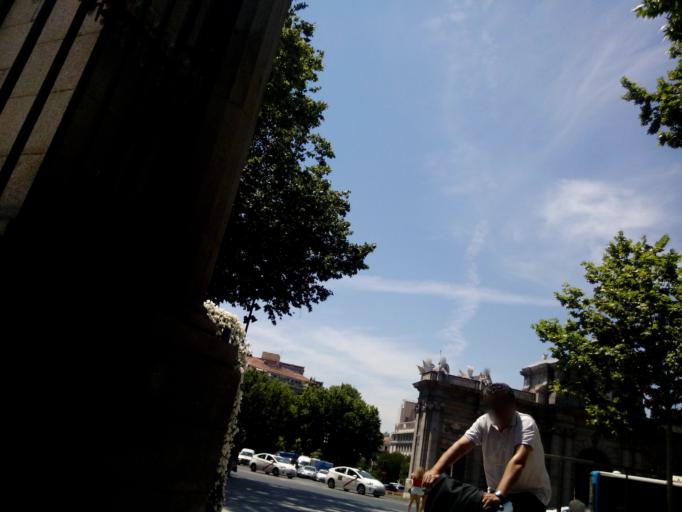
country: ES
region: Madrid
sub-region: Provincia de Madrid
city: Retiro
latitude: 40.4194
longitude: -3.6878
